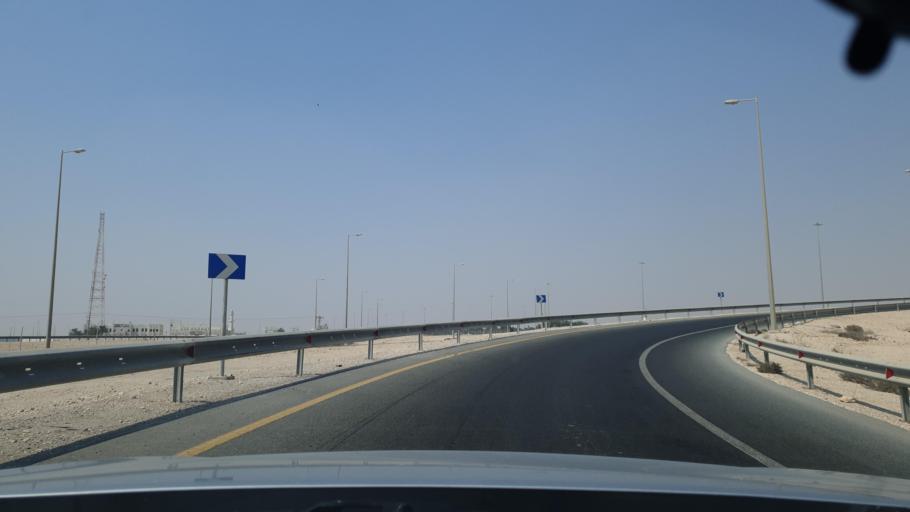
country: QA
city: Al Ghuwayriyah
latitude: 25.8278
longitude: 51.3486
